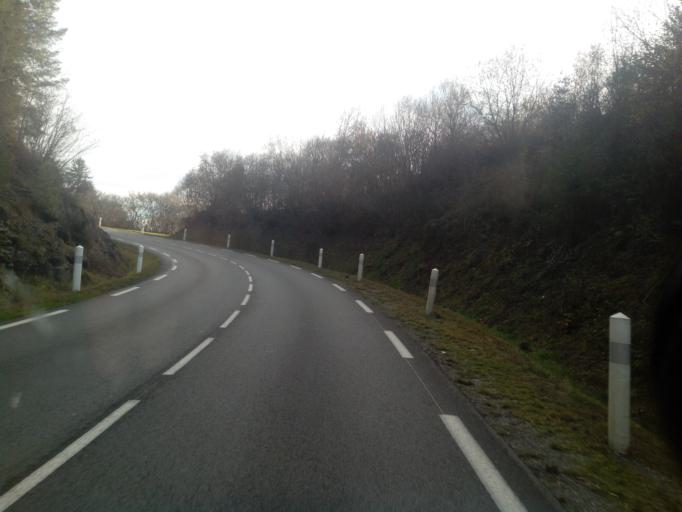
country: FR
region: Limousin
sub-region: Departement de la Haute-Vienne
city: Linards
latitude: 45.7664
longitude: 1.5553
